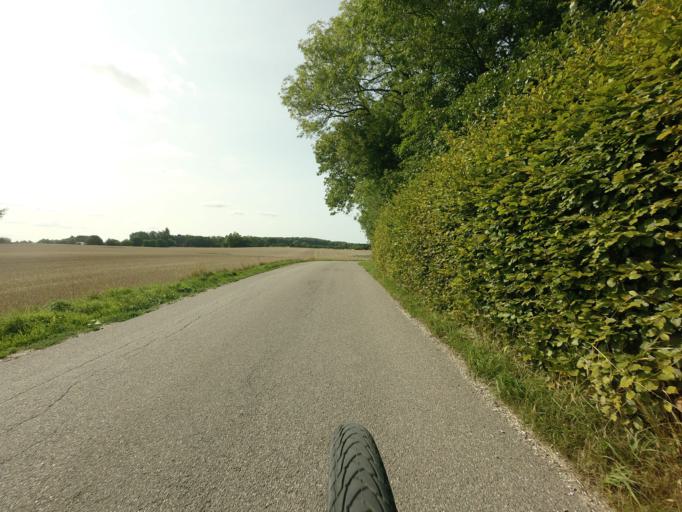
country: DK
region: Zealand
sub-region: Faxe Kommune
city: Fakse
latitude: 55.2111
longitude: 12.1321
